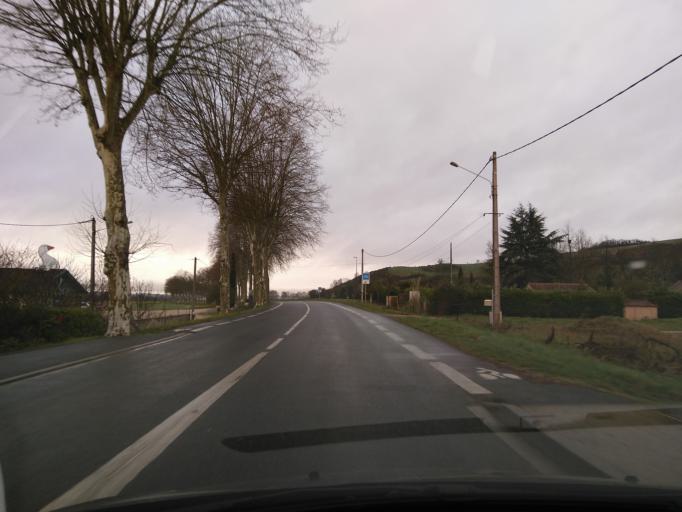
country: FR
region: Midi-Pyrenees
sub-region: Departement de la Haute-Garonne
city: Montesquieu-Volvestre
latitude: 43.2190
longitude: 1.2186
